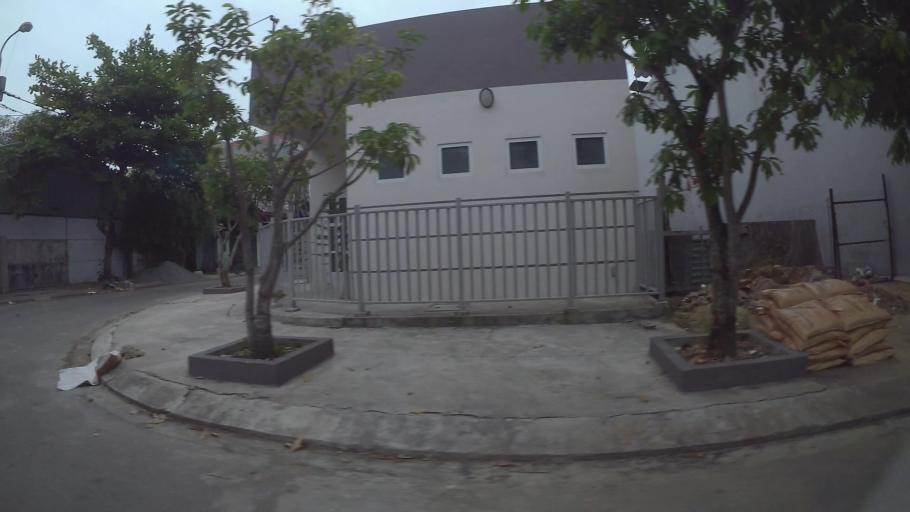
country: VN
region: Da Nang
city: Thanh Khe
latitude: 16.0521
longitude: 108.1791
